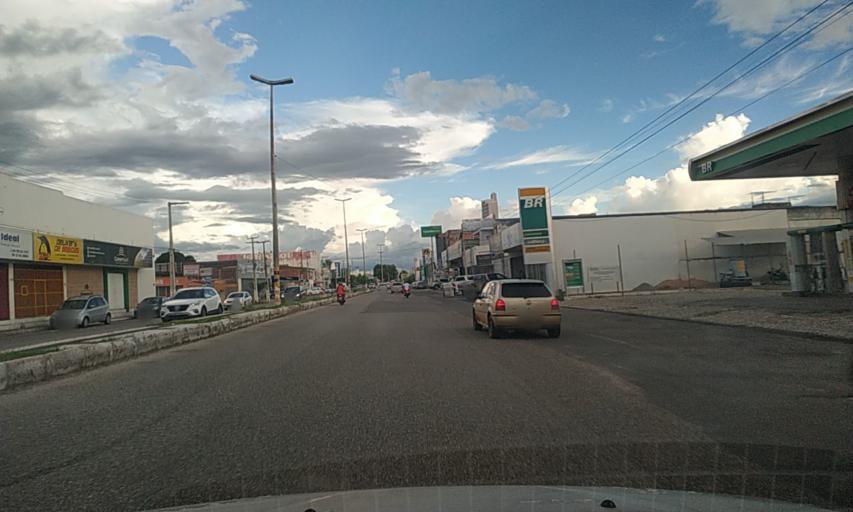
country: BR
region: Rio Grande do Norte
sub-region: Mossoro
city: Mossoro
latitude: -5.1978
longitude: -37.3407
